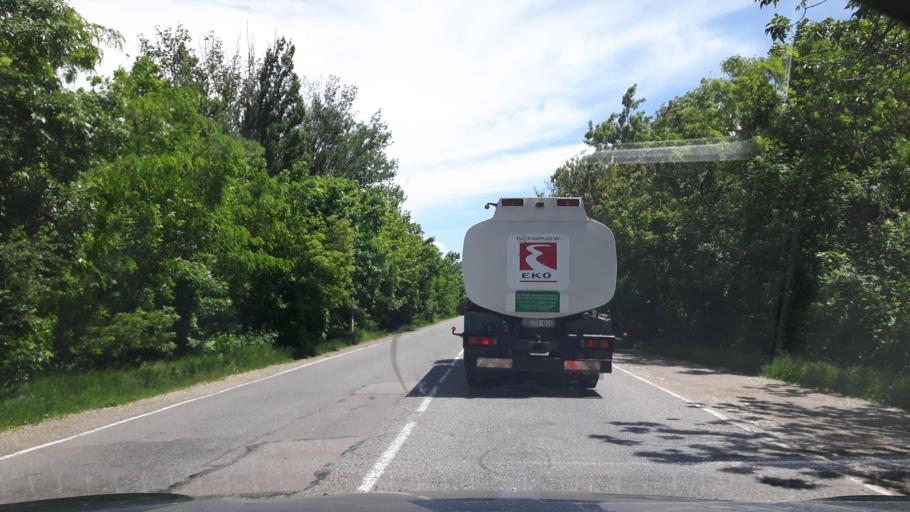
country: GE
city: Didi Lilo
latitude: 41.6968
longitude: 45.0978
